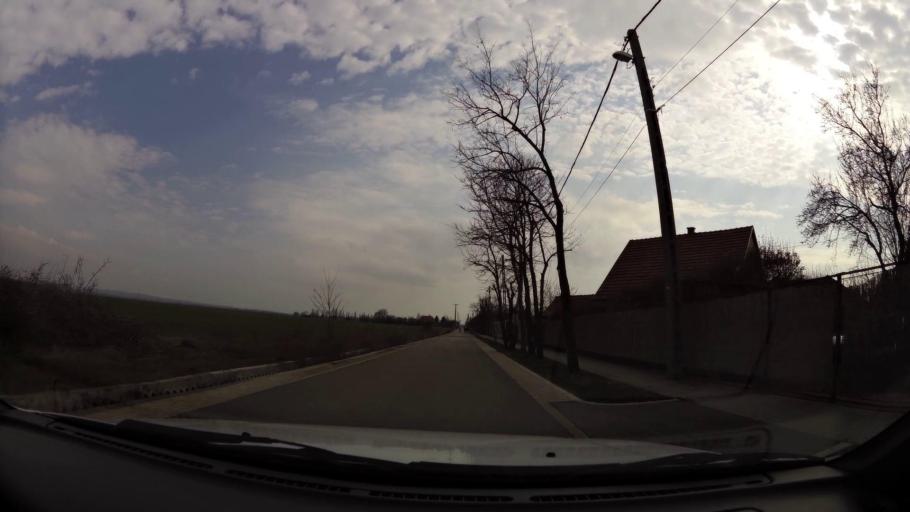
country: HU
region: Pest
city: Csomor
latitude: 47.5275
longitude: 19.2366
